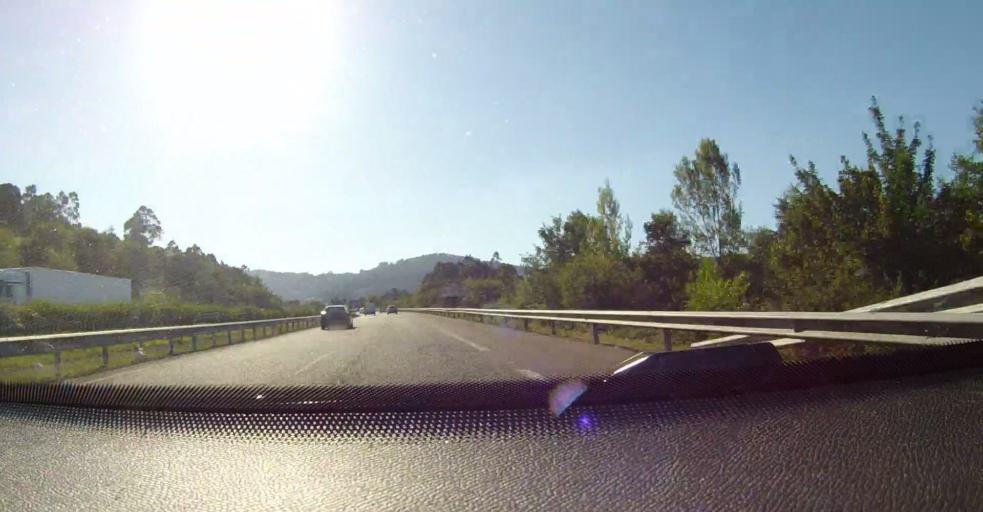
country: ES
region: Asturias
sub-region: Province of Asturias
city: Villaviciosa
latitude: 43.5005
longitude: -5.4047
